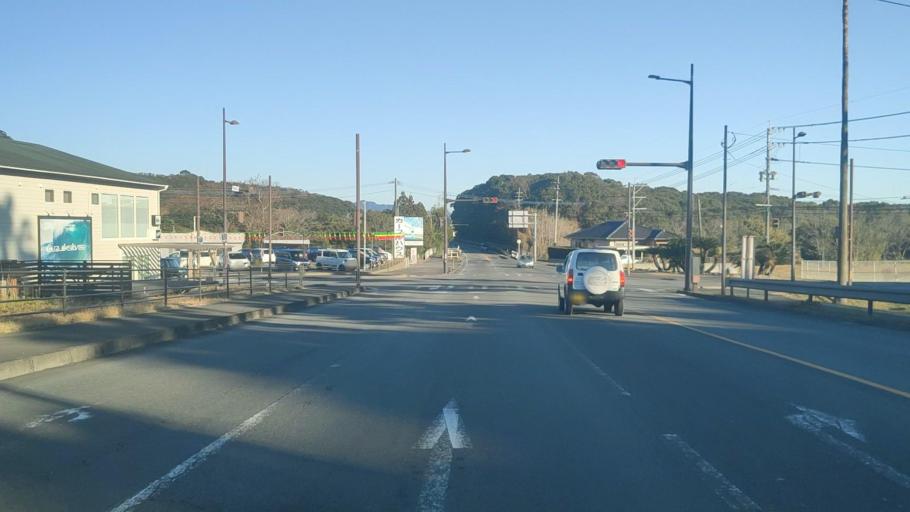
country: JP
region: Miyazaki
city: Nobeoka
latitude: 32.3792
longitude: 131.6276
